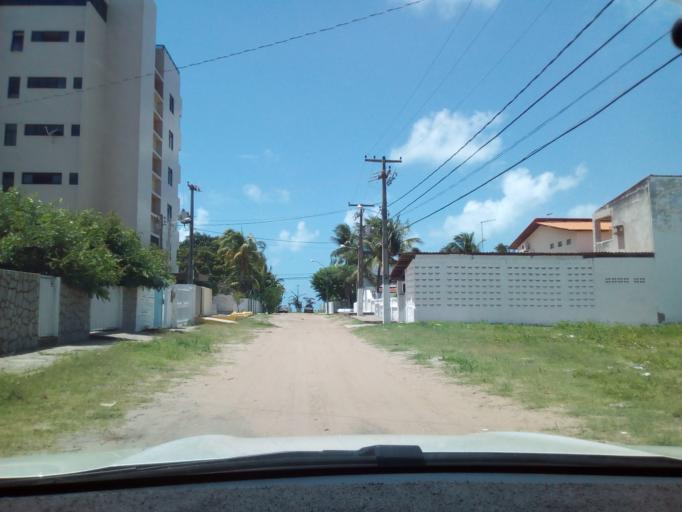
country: BR
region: Paraiba
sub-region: Cabedelo
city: Cabedelo
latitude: -7.0015
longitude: -34.8271
